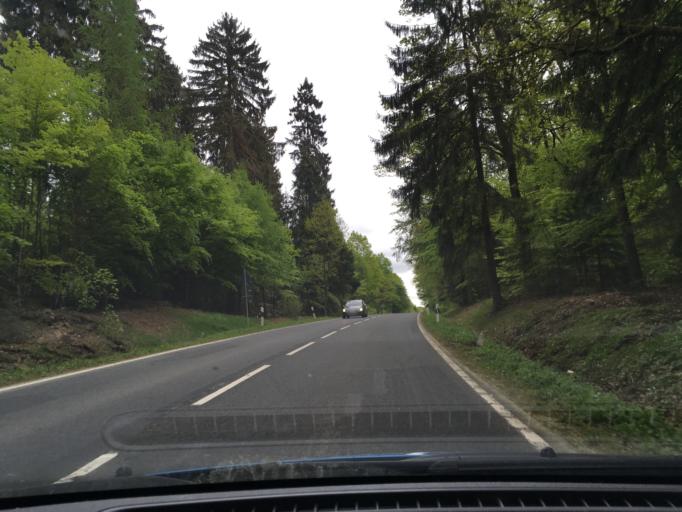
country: DE
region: Lower Saxony
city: Derental
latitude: 51.6907
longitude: 9.4836
